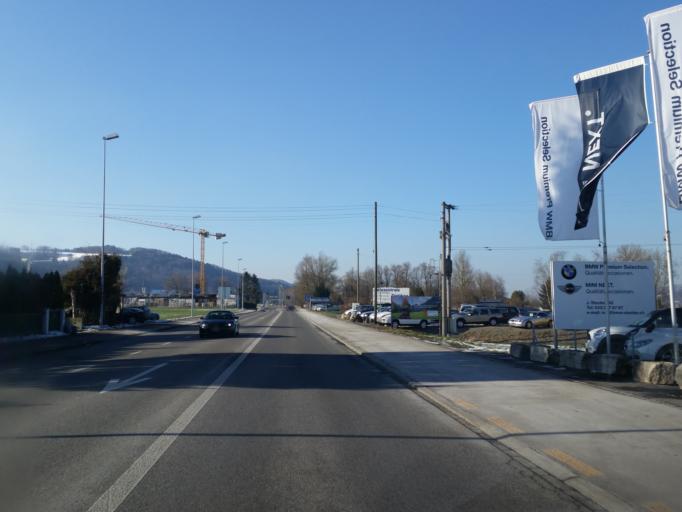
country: CH
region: Zurich
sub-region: Bezirk Dietikon
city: Dietikon / Almend
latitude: 47.4101
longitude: 8.3888
